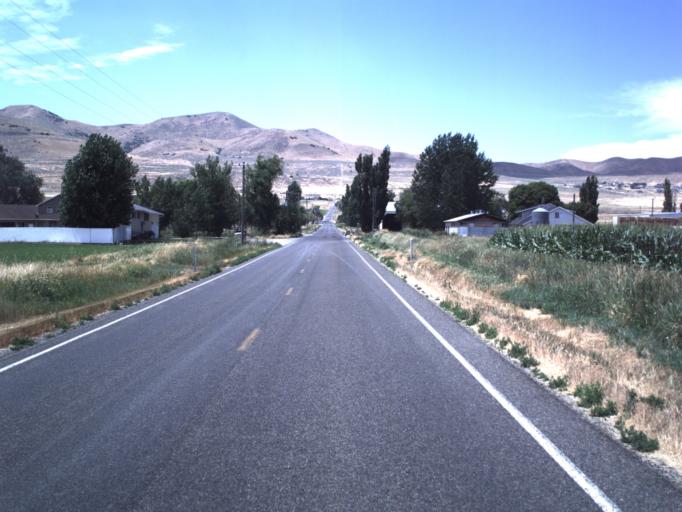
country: US
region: Utah
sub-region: Box Elder County
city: Tremonton
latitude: 41.6946
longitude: -112.2851
